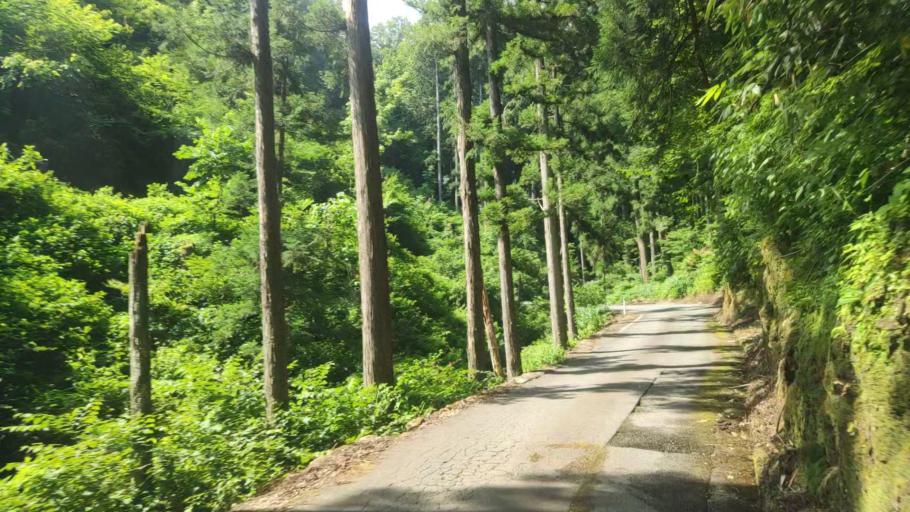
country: JP
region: Ishikawa
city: Komatsu
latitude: 36.2985
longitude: 136.5283
